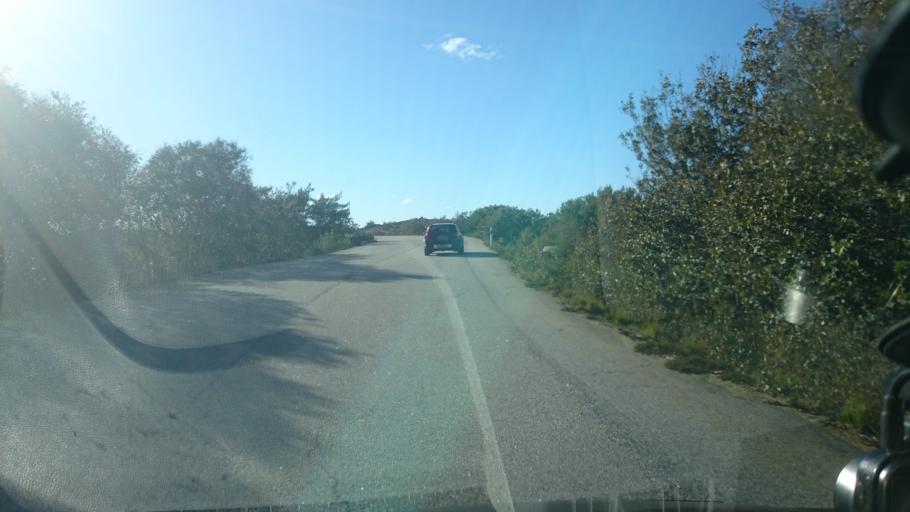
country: SE
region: Vaestra Goetaland
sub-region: Lysekils Kommun
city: Lysekil
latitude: 58.3193
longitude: 11.4122
